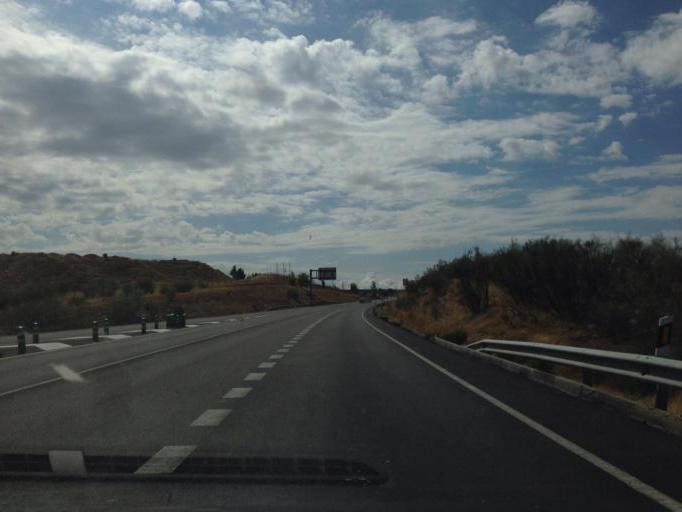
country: ES
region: Madrid
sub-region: Provincia de Madrid
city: Cobena
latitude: 40.5651
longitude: -3.5175
